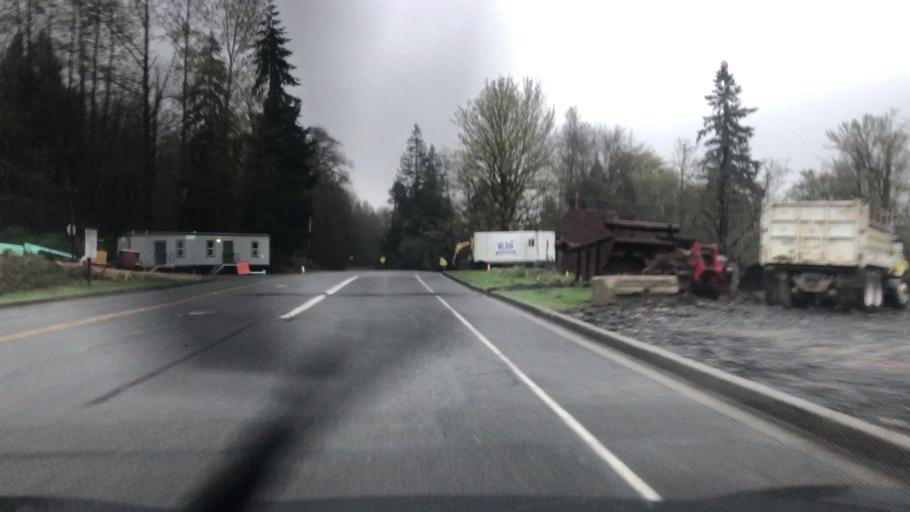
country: US
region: Washington
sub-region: King County
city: Duvall
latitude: 47.7263
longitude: -121.9811
